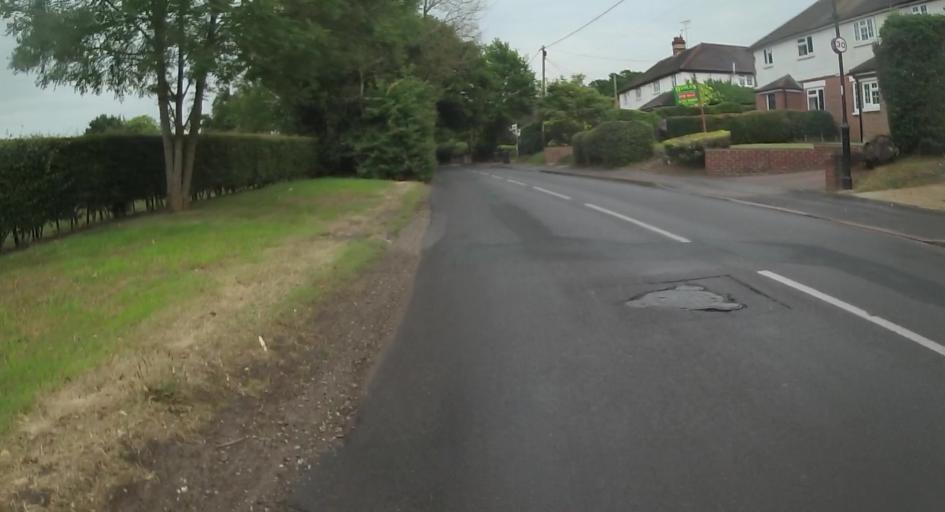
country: GB
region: England
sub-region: Hampshire
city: Fleet
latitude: 51.2654
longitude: -0.8580
